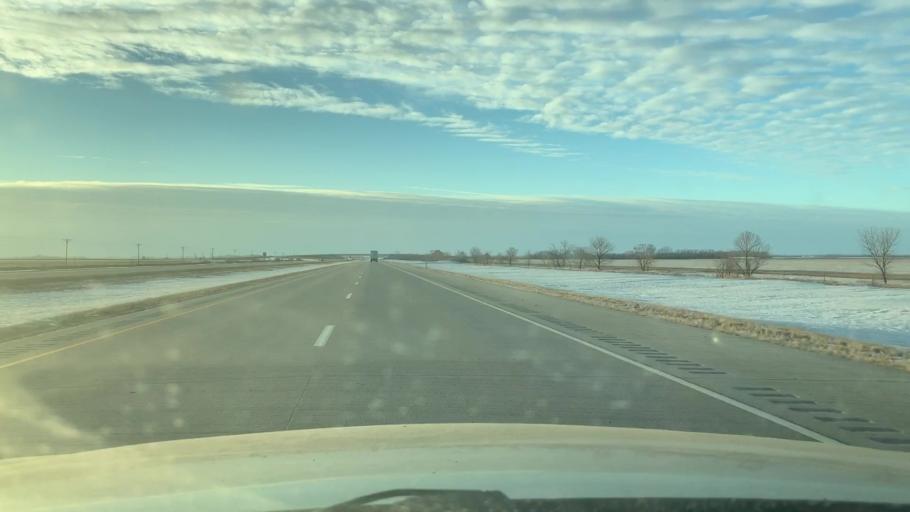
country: US
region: North Dakota
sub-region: Cass County
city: Casselton
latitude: 46.8758
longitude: -97.3290
